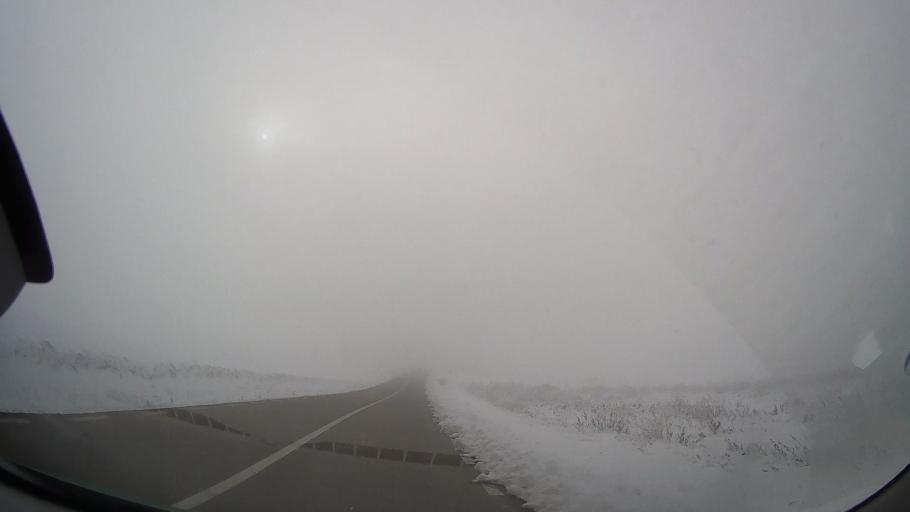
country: RO
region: Iasi
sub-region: Comuna Valea Seaca
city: Topile
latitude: 47.2720
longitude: 26.6703
